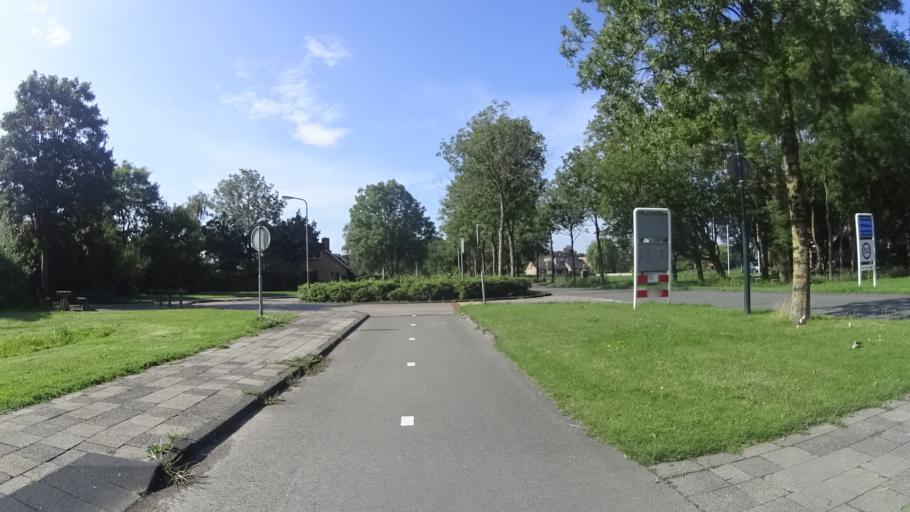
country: NL
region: Friesland
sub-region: Menameradiel
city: Dronryp
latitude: 53.1996
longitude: 5.6487
